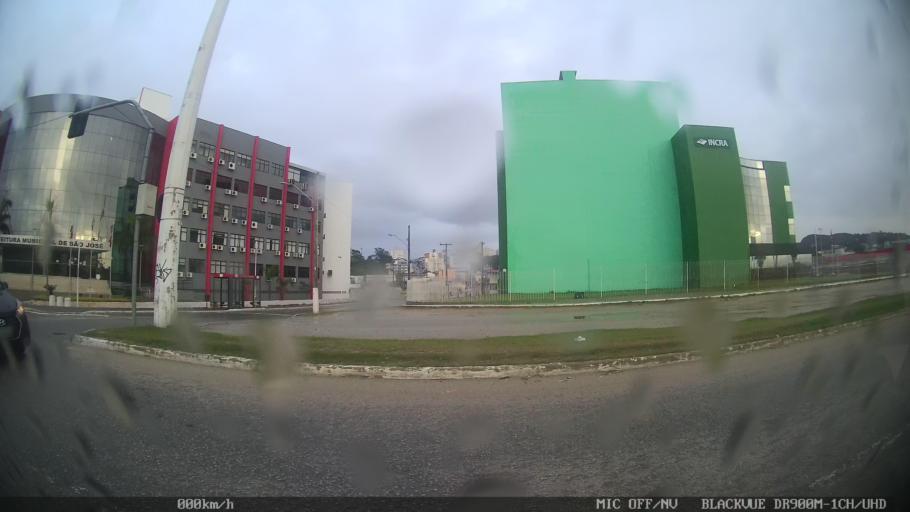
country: BR
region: Santa Catarina
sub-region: Sao Jose
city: Campinas
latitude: -27.6087
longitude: -48.6264
